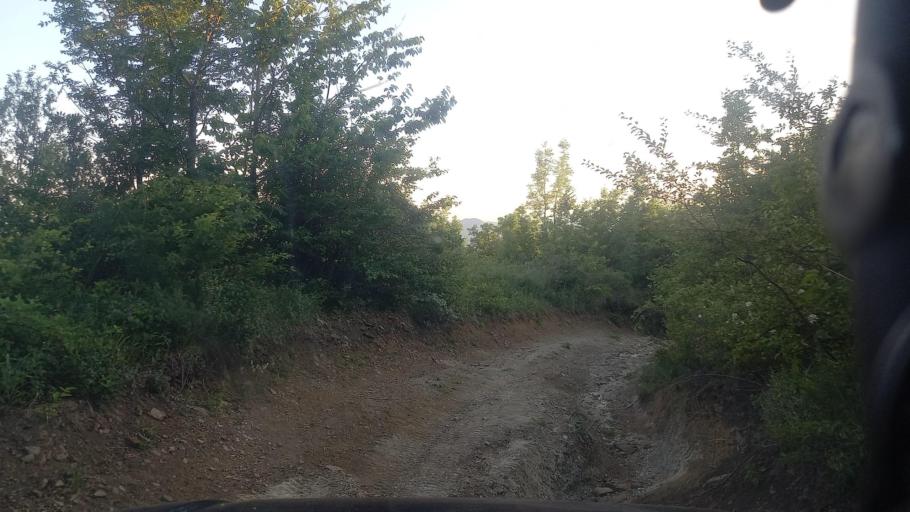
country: RU
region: Krasnodarskiy
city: Pshada
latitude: 44.5941
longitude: 38.2828
